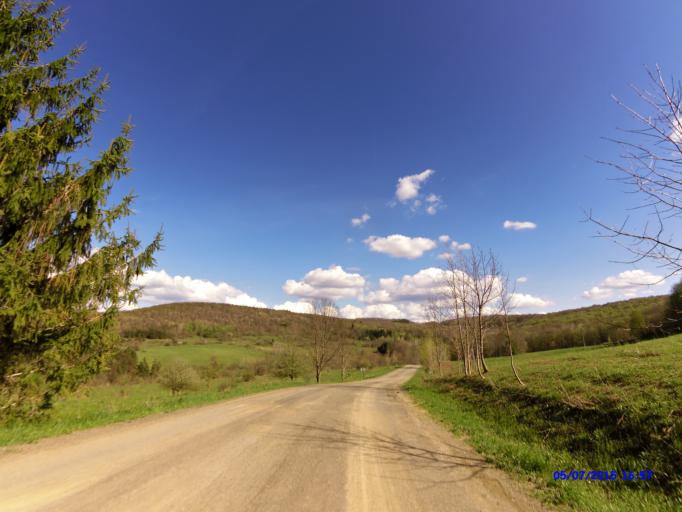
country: US
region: New York
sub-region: Cattaraugus County
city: Little Valley
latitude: 42.3009
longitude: -78.7502
